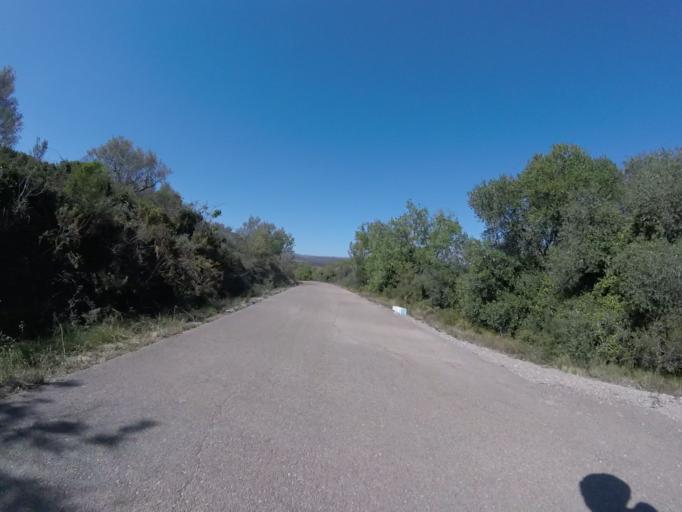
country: ES
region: Valencia
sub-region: Provincia de Castello
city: Cuevas de Vinroma
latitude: 40.3838
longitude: 0.1504
